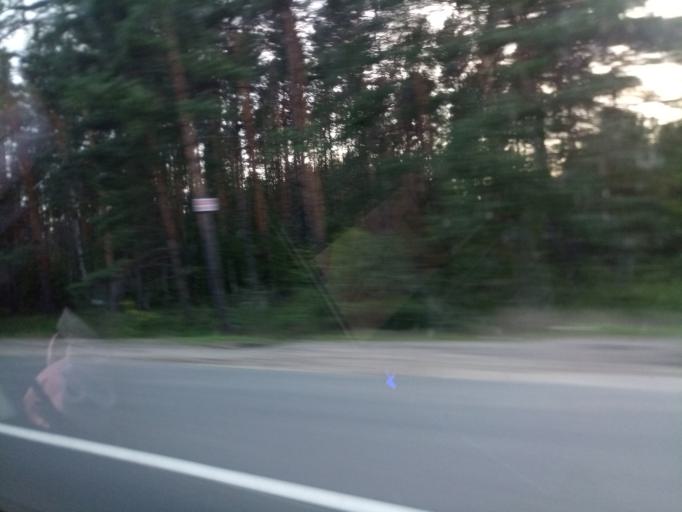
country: RU
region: Moskovskaya
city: Noginsk-9
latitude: 56.1017
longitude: 38.5850
